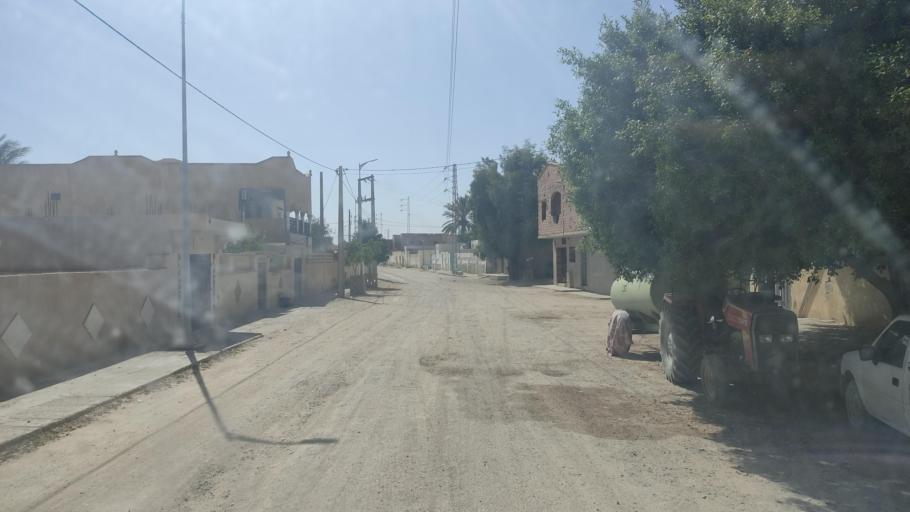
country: TN
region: Gafsa
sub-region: Gafsa Municipality
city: Gafsa
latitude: 34.3366
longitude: 8.9218
